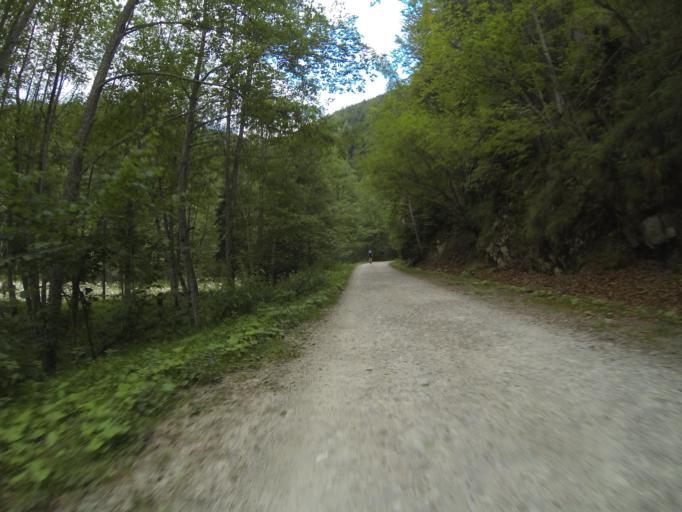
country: RO
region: Gorj
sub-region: Comuna Polovragi
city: Polovragi
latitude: 45.2775
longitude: 23.7732
